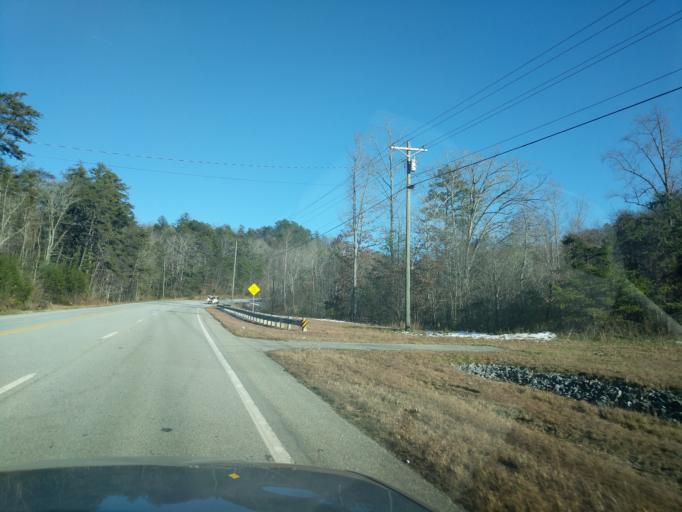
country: US
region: Georgia
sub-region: Rabun County
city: Clayton
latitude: 34.8678
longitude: -83.5270
